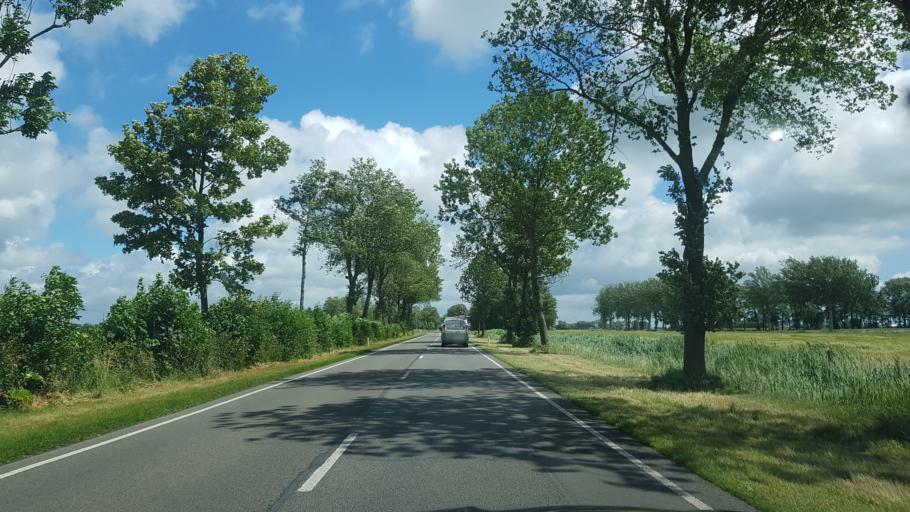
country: NL
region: Groningen
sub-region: Gemeente Bedum
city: Bedum
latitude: 53.4071
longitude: 6.6217
